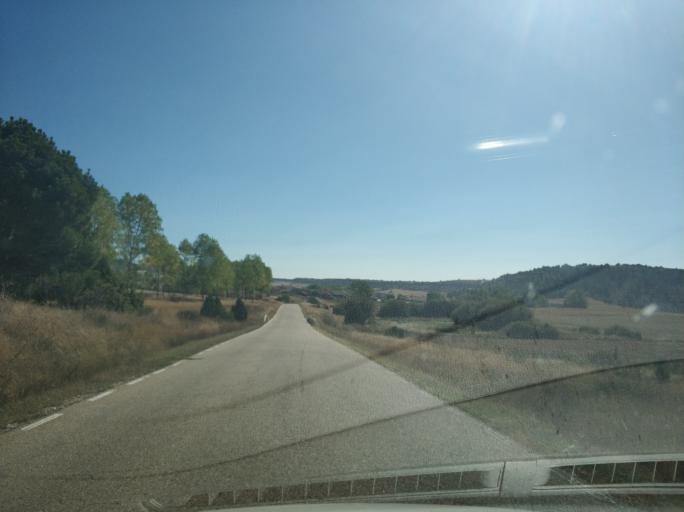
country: ES
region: Castille and Leon
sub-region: Provincia de Soria
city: Santa Maria de las Hoyas
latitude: 41.7742
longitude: -3.1767
